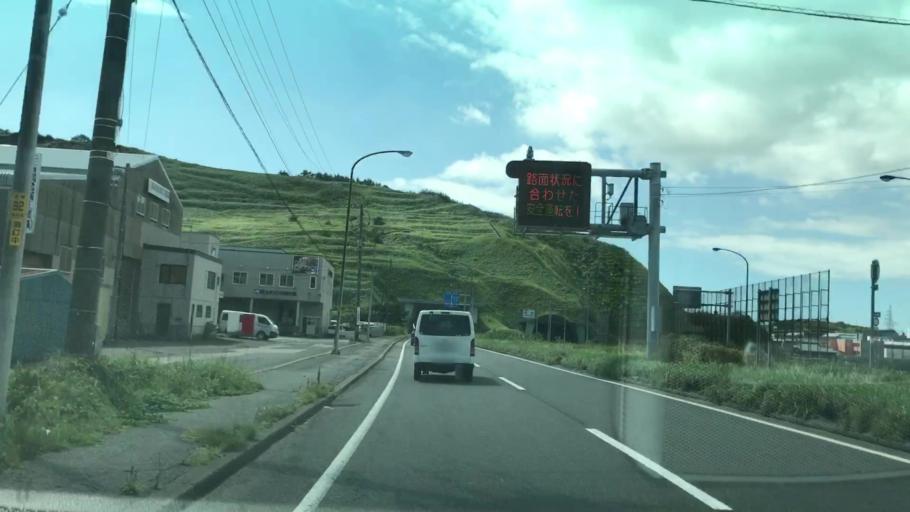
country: JP
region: Hokkaido
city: Muroran
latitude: 42.3433
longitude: 141.0340
